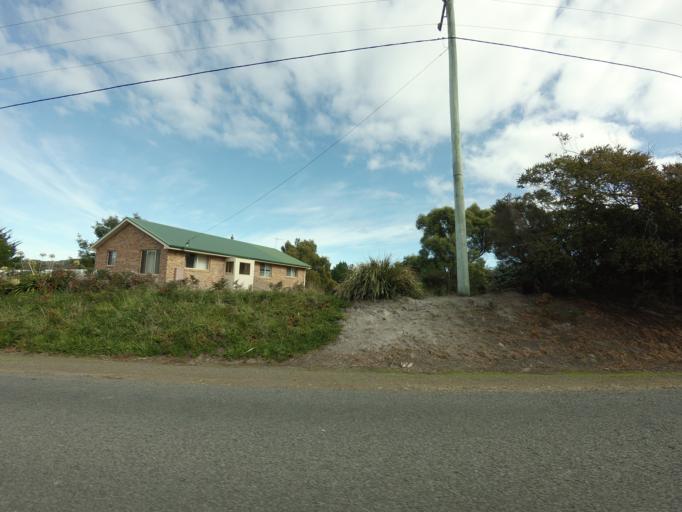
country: AU
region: Tasmania
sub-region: Clarence
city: Sandford
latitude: -43.0916
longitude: 147.7388
